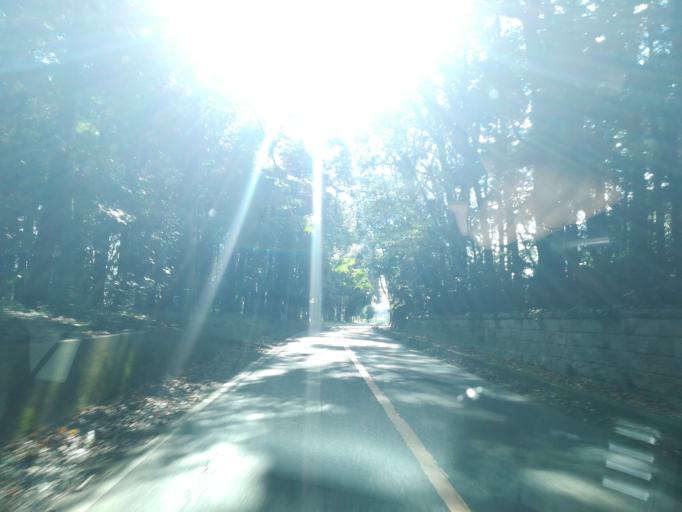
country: JP
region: Ibaraki
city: Naka
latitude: 36.0667
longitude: 140.0891
